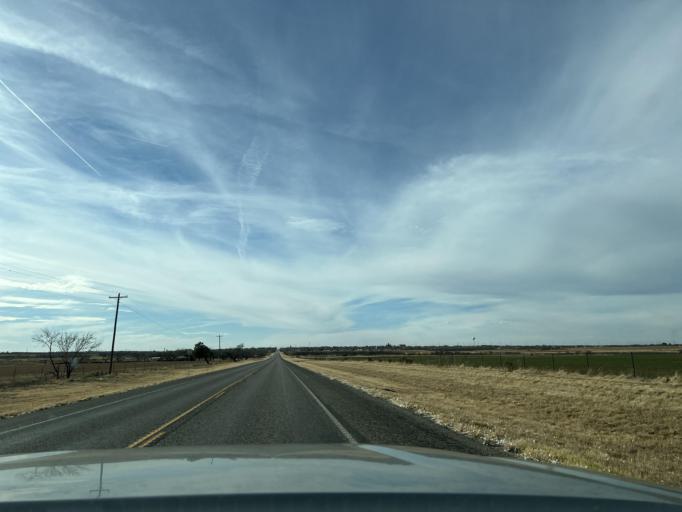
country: US
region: Texas
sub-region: Jones County
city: Anson
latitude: 32.7514
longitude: -99.8694
